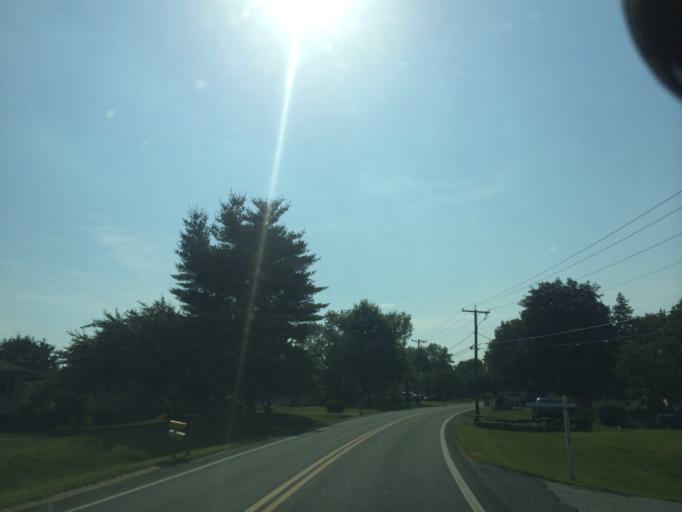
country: US
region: Maryland
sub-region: Carroll County
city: Eldersburg
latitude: 39.4322
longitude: -76.9669
